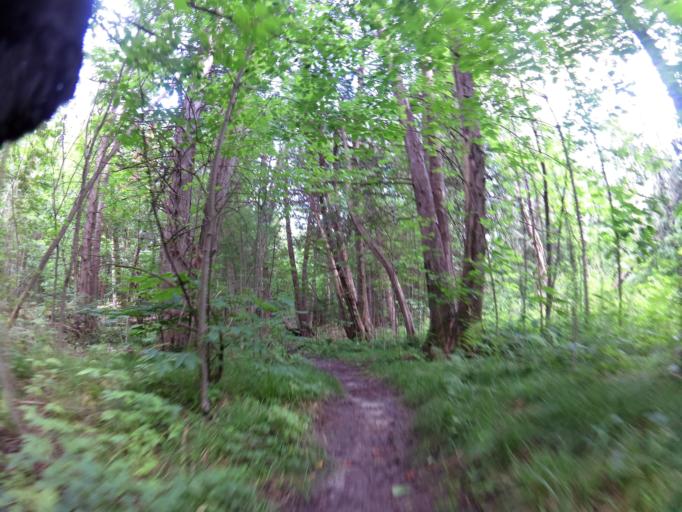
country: CA
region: Ontario
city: Bells Corners
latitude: 45.0305
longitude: -75.6600
